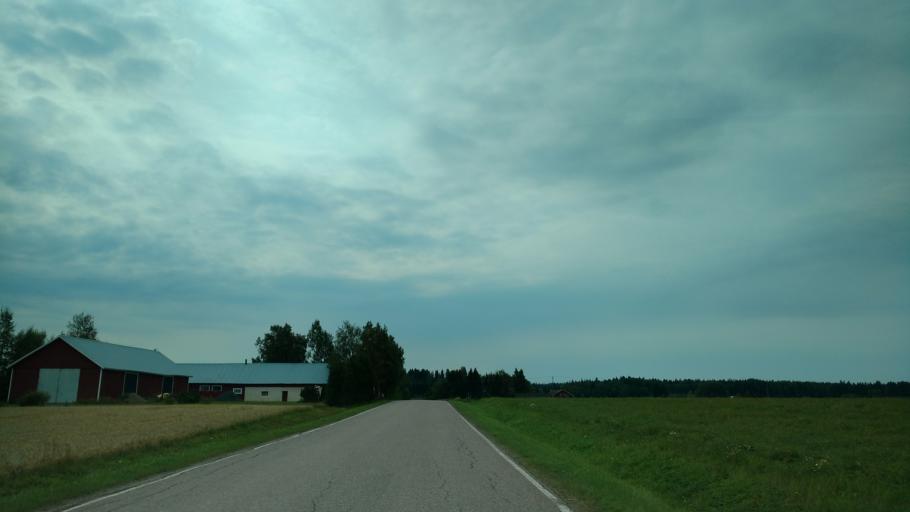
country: FI
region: Haeme
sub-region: Forssa
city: Ypaejae
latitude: 60.7875
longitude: 23.2708
